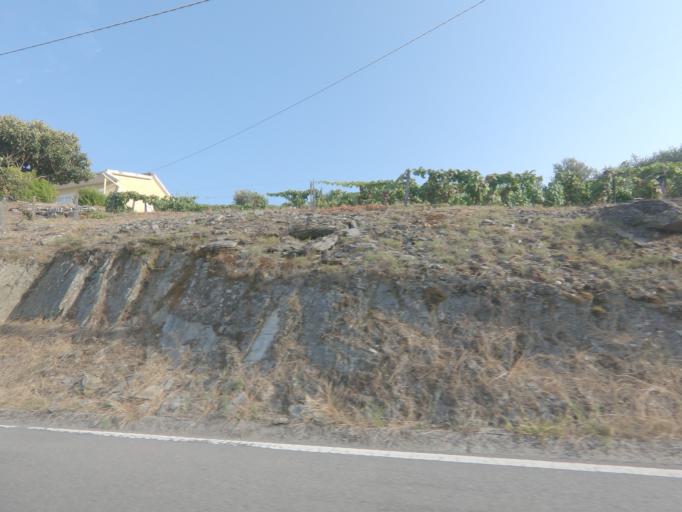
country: PT
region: Viseu
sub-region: Tabuaco
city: Tabuaco
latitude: 41.1419
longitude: -7.6069
